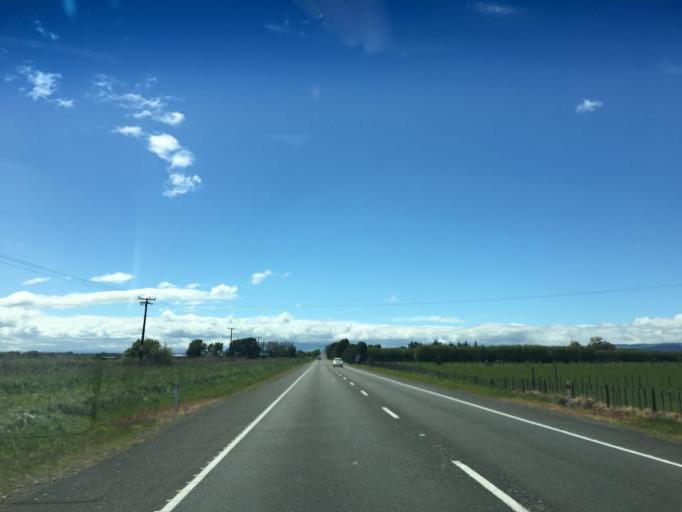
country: NZ
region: Manawatu-Wanganui
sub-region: Palmerston North City
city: Palmerston North
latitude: -40.3893
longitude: 175.5304
